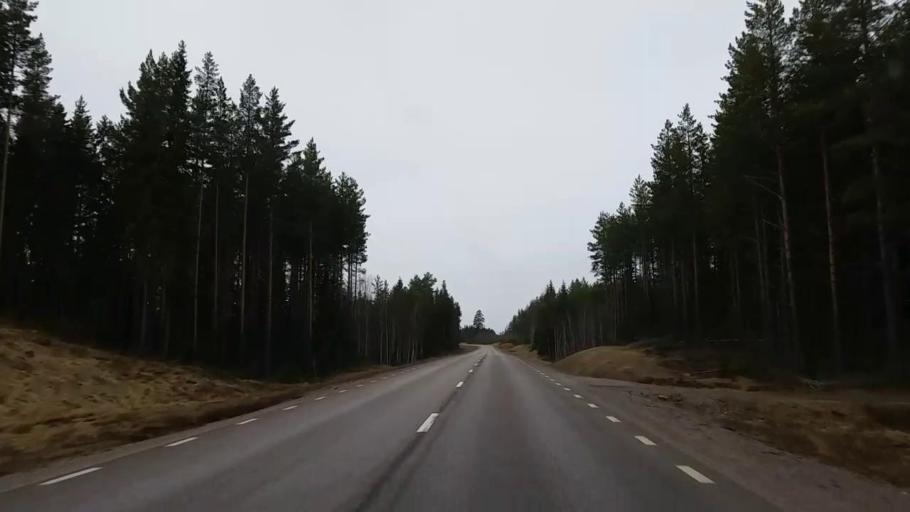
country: SE
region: Gaevleborg
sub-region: Ovanakers Kommun
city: Edsbyn
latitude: 61.1820
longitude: 15.8786
